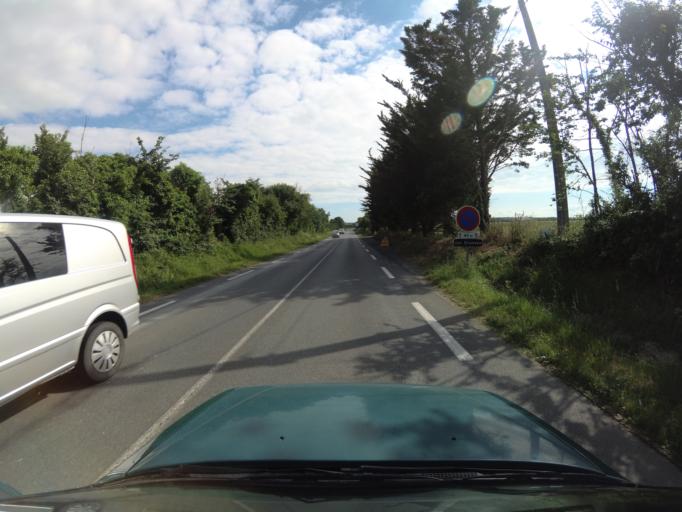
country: FR
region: Poitou-Charentes
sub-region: Departement de la Charente-Maritime
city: Saint-Xandre
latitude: 46.2229
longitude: -1.0851
